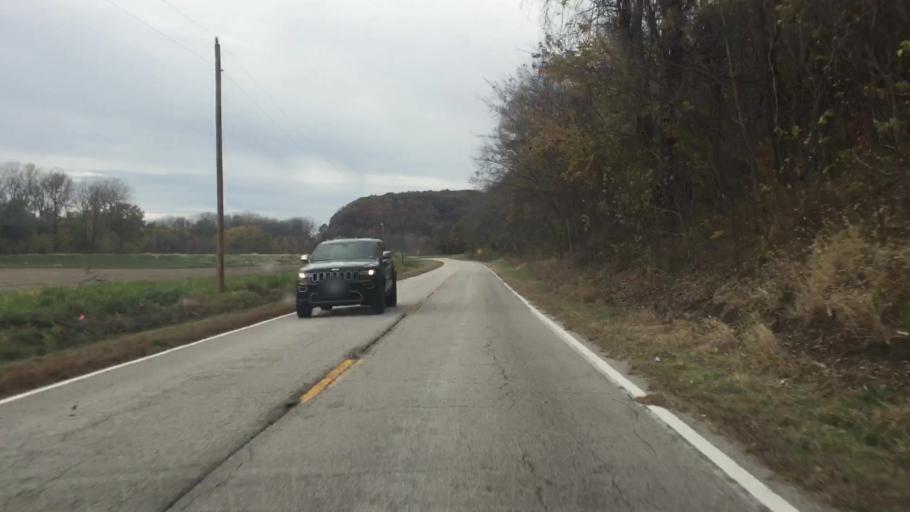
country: US
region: Missouri
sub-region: Gasconade County
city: Hermann
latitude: 38.7050
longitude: -91.6191
